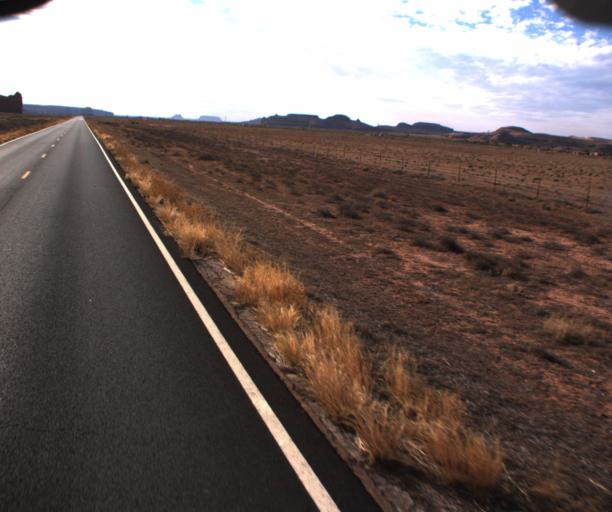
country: US
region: Arizona
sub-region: Apache County
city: Many Farms
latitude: 36.7557
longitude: -109.6467
